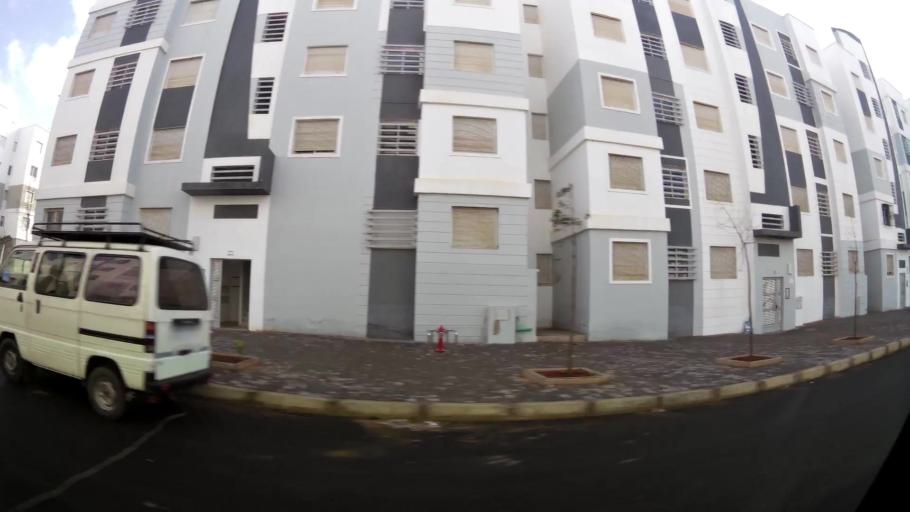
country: MA
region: Grand Casablanca
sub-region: Casablanca
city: Casablanca
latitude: 33.5535
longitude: -7.7053
